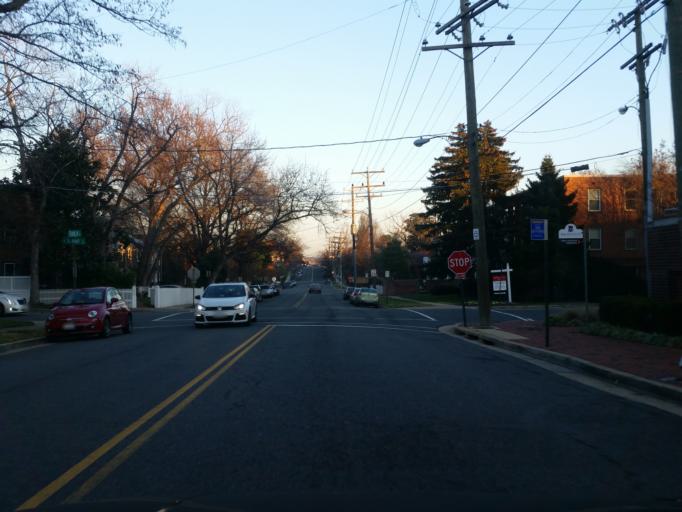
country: US
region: Virginia
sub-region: City of Alexandria
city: Alexandria
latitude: 38.7982
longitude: -77.0478
